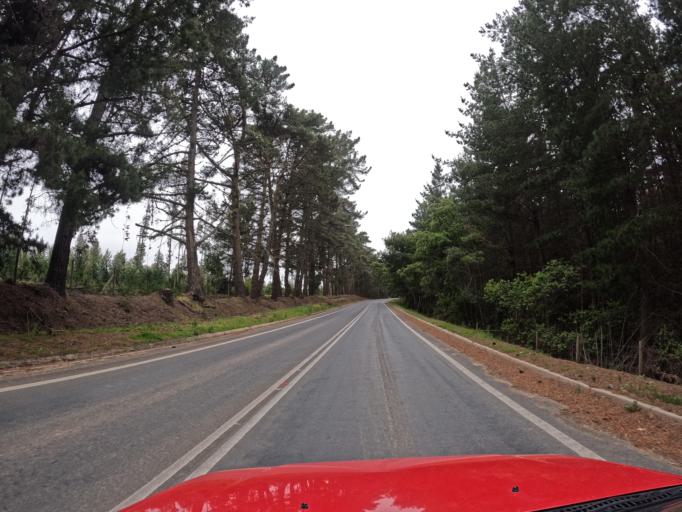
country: CL
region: O'Higgins
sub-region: Provincia de Colchagua
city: Santa Cruz
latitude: -34.5773
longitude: -72.0163
